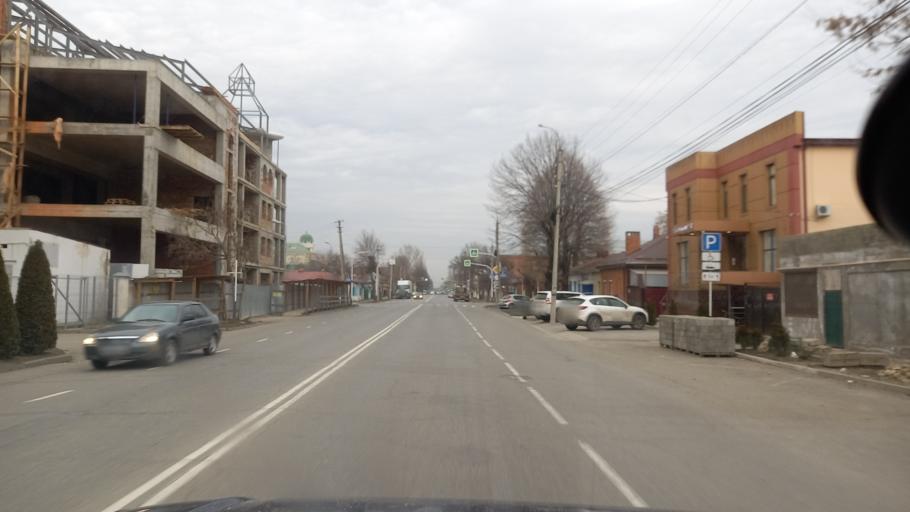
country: RU
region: Adygeya
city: Maykop
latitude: 44.6012
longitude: 40.1103
